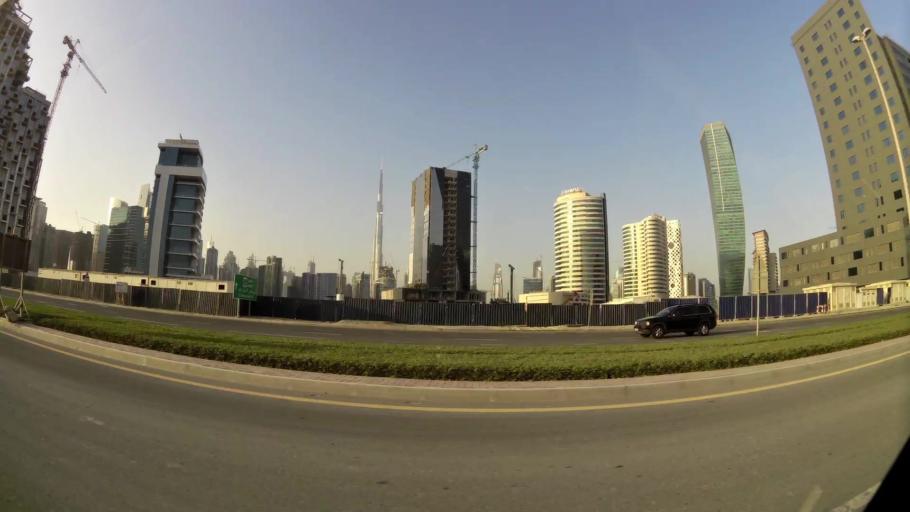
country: AE
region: Dubai
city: Dubai
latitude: 25.1786
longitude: 55.2652
